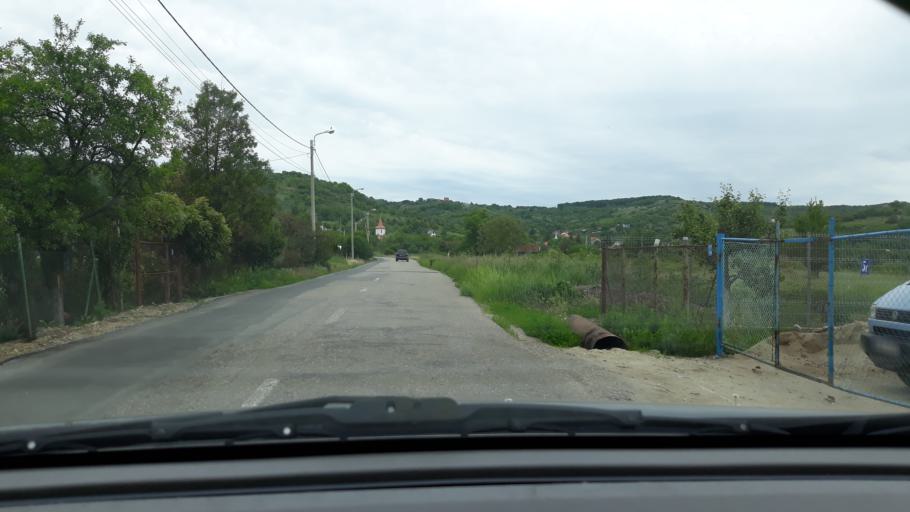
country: RO
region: Bihor
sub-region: Comuna Osorheiu
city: Alparea
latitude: 47.0554
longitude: 22.0014
